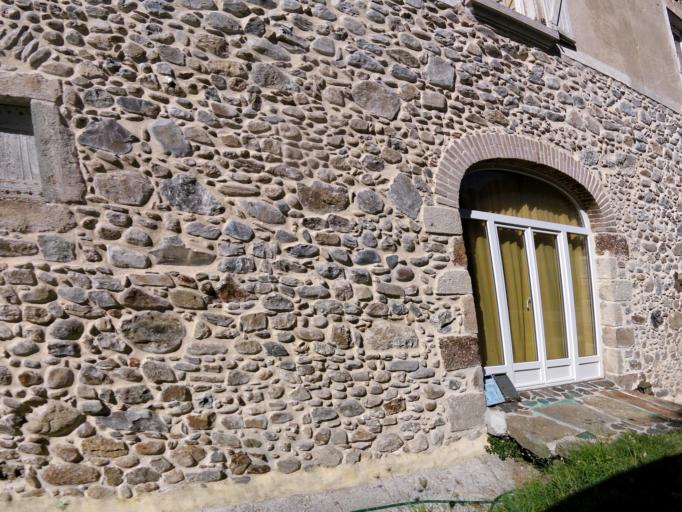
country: FR
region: Languedoc-Roussillon
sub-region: Departement du Gard
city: Saint-Jean-du-Gard
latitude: 44.1132
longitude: 3.8567
